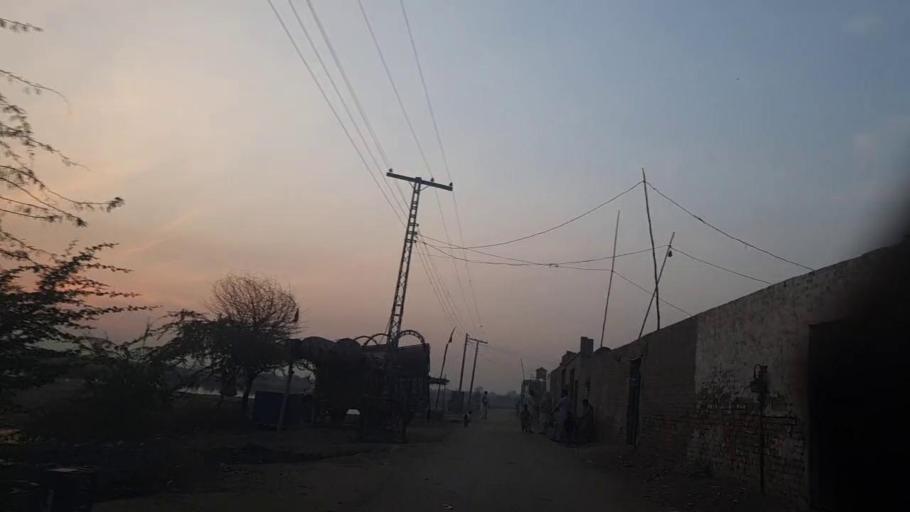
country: PK
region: Sindh
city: Sakrand
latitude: 26.1009
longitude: 68.3120
